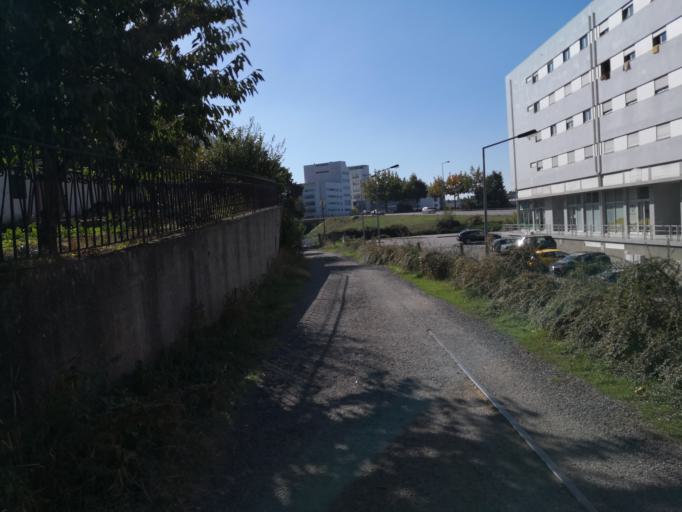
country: PT
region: Vila Real
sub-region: Vila Real
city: Vila Real
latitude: 41.2983
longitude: -7.7316
